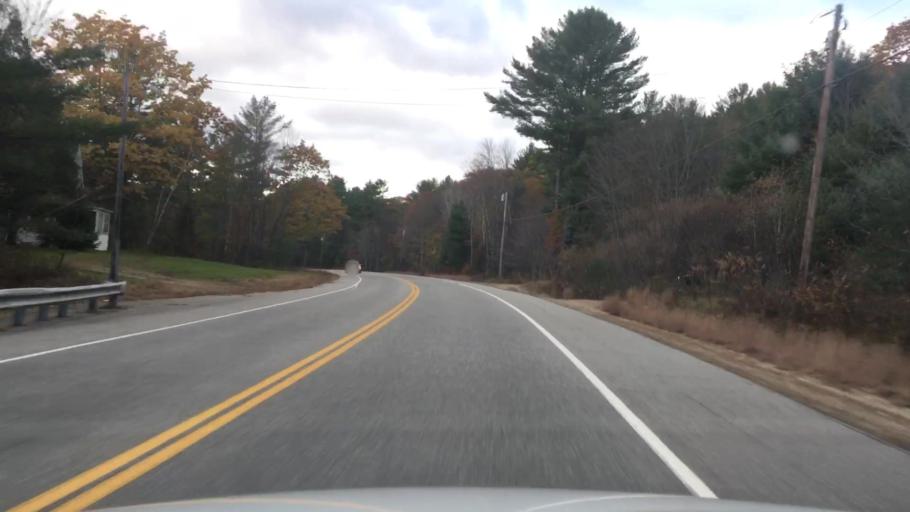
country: US
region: Maine
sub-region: Androscoggin County
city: Livermore
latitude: 44.4042
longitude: -70.2665
